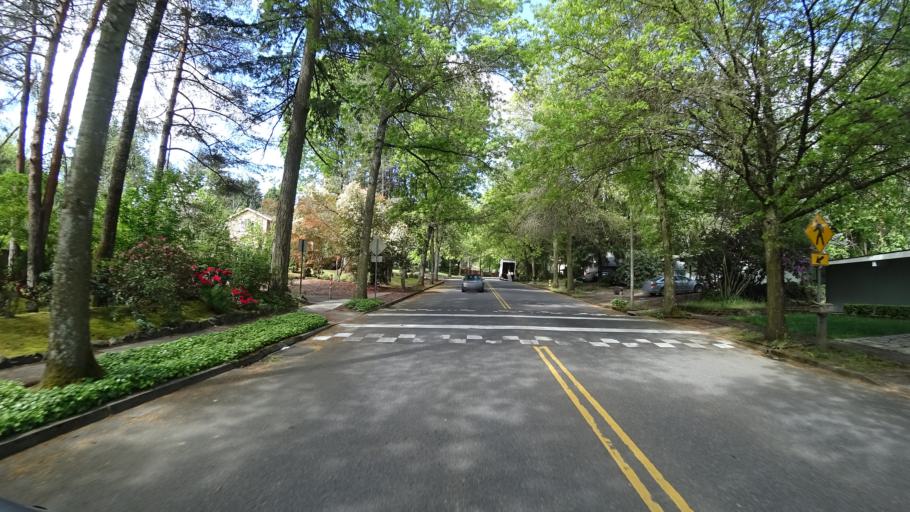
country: US
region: Oregon
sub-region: Washington County
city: Beaverton
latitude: 45.4665
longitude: -122.8118
